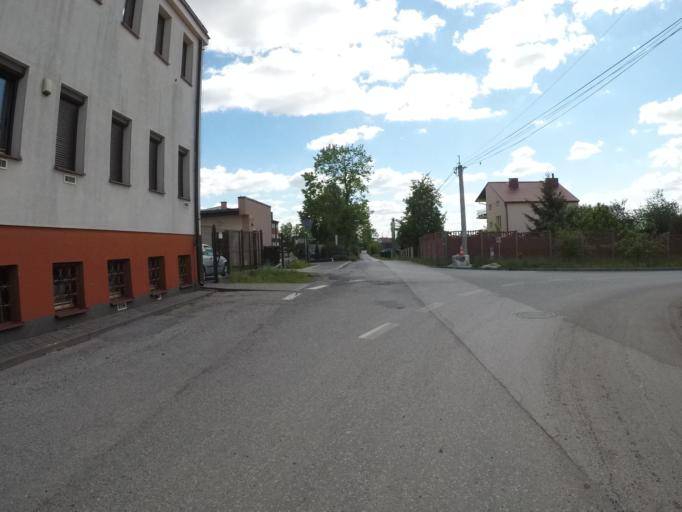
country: PL
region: Swietokrzyskie
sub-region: Powiat kielecki
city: Kostomloty Pierwsze
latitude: 50.9069
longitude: 20.5903
